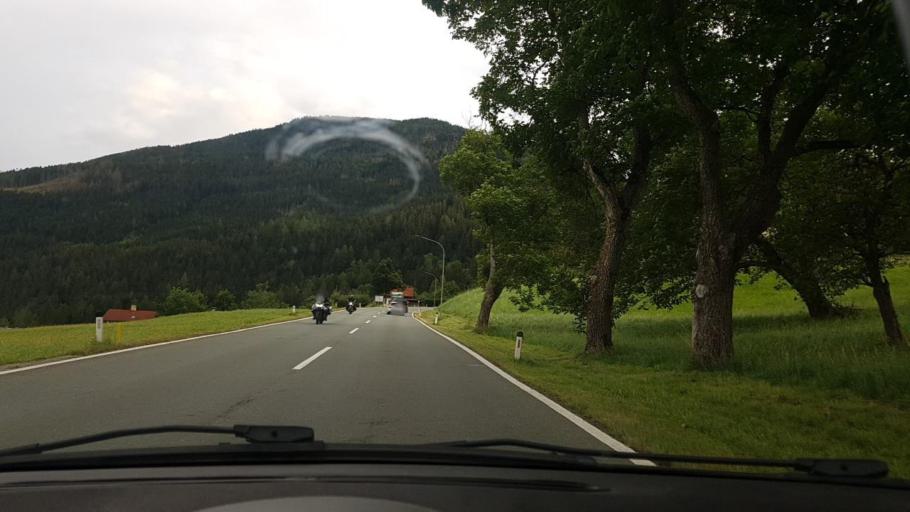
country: AT
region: Carinthia
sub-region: Politischer Bezirk Spittal an der Drau
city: Winklern
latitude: 46.8678
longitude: 12.8755
